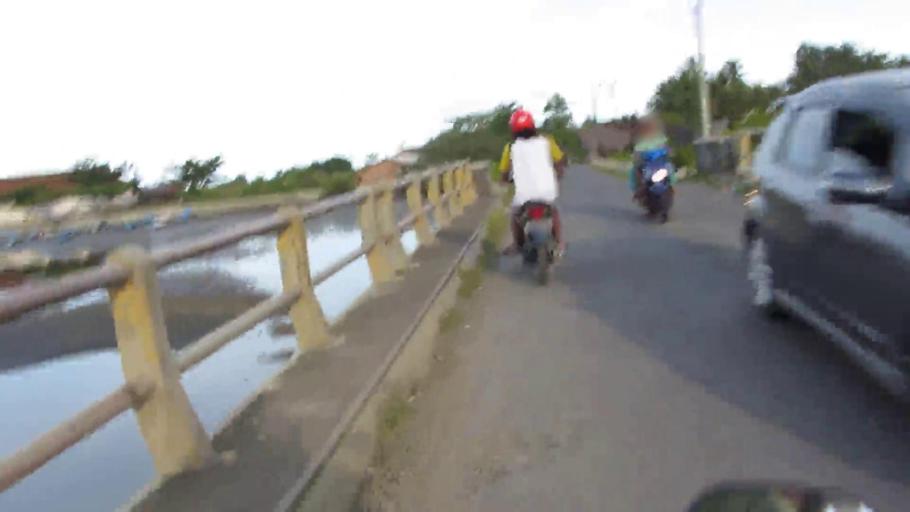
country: ID
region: West Java
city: Karangjaladri
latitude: -7.7130
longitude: 108.4990
